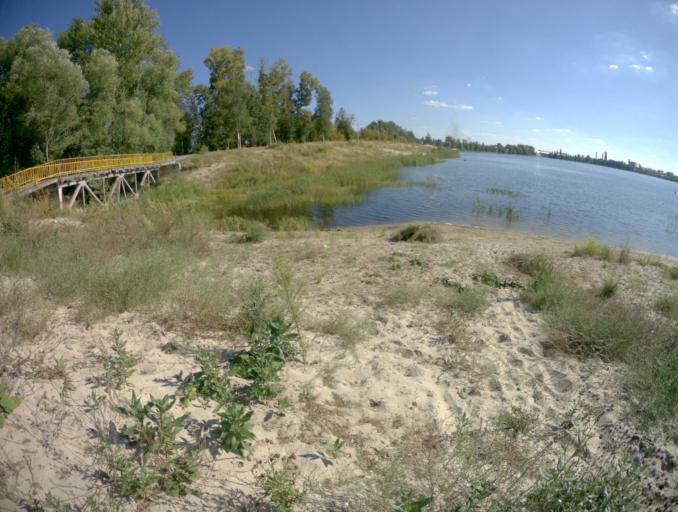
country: RU
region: Vladimir
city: Gus'-Khrustal'nyy
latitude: 55.6249
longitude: 40.6717
